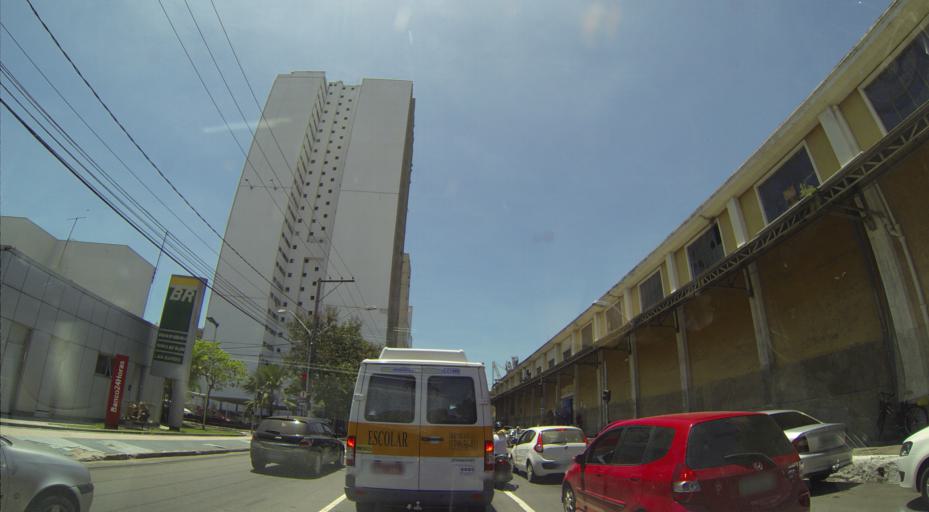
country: BR
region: Espirito Santo
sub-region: Vitoria
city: Vitoria
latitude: -20.3217
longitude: -40.3433
